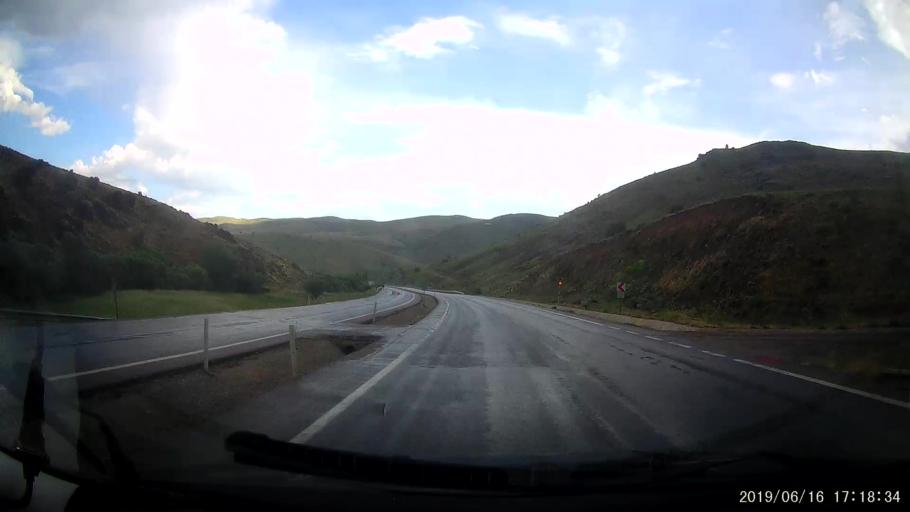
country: TR
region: Erzincan
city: Tercan
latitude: 39.8121
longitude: 40.5288
